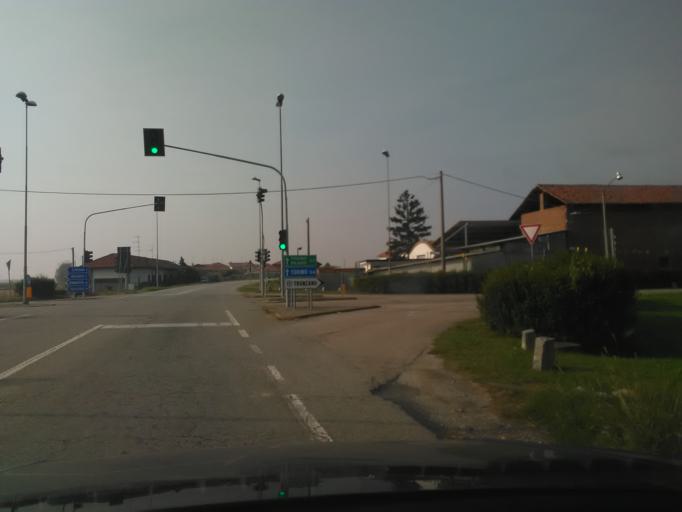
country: IT
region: Piedmont
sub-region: Provincia di Vercelli
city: Tronzano Vercellese
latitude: 45.3390
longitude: 8.1797
